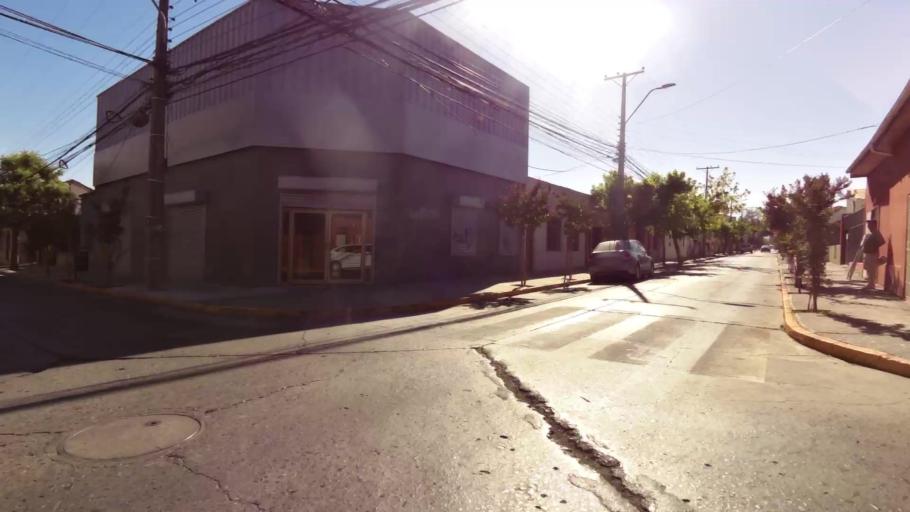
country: CL
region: O'Higgins
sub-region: Provincia de Cachapoal
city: Rancagua
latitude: -34.1675
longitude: -70.7360
